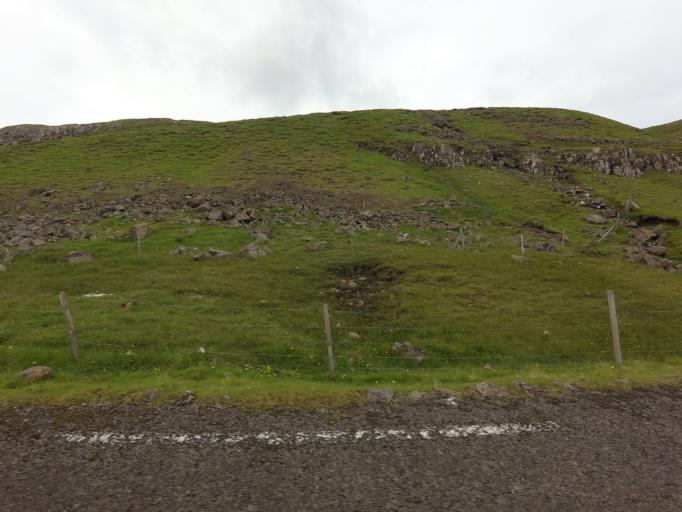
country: FO
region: Suduroy
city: Vagur
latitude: 61.4412
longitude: -6.7329
